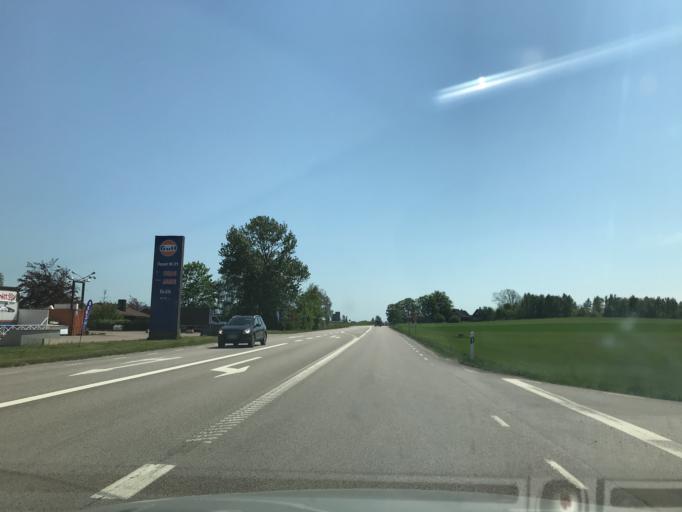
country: SE
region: Skane
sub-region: Astorps Kommun
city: Kvidinge
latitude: 56.1870
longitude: 13.0564
